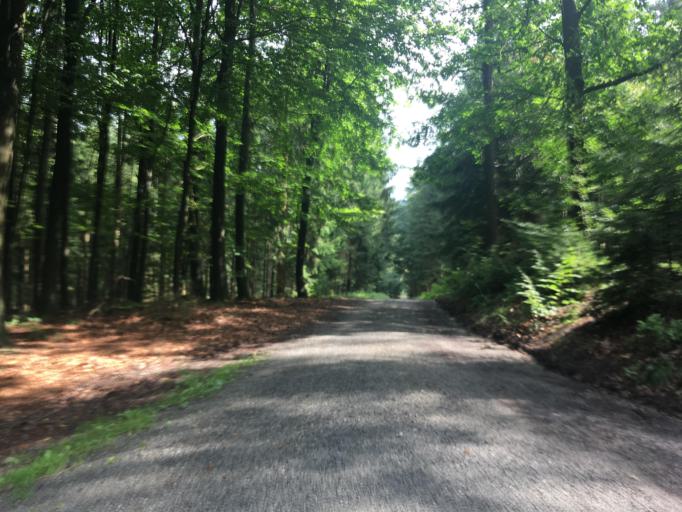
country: DE
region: Saxony
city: Bad Schandau
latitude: 50.9123
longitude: 14.2129
